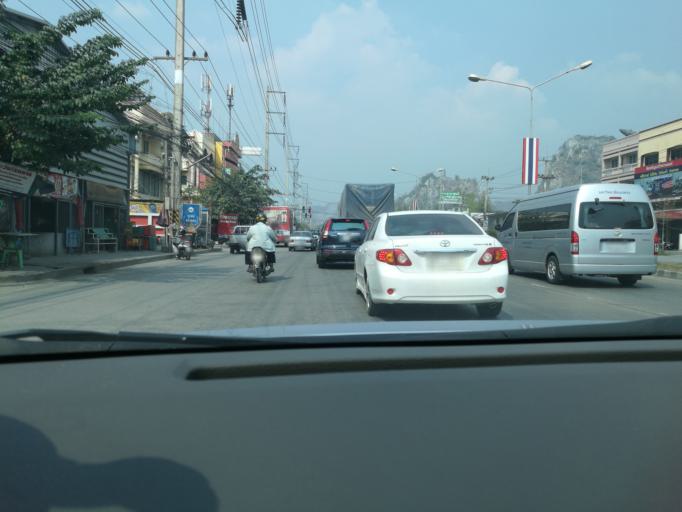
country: TH
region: Sara Buri
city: Phra Phutthabat
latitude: 14.6897
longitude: 100.8698
